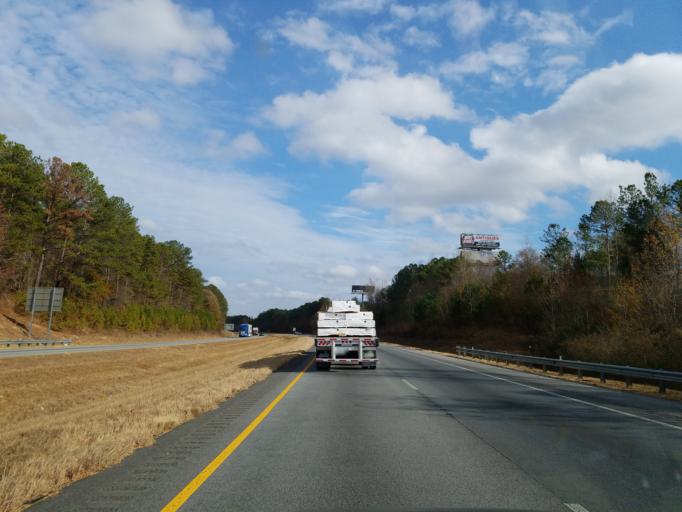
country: US
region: Alabama
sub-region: Cleburne County
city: Heflin
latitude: 33.6204
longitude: -85.5870
